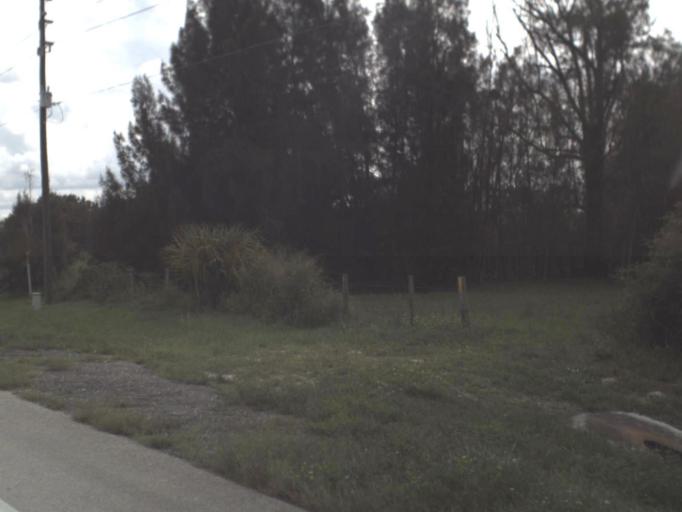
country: US
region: Florida
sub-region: DeSoto County
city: Southeast Arcadia
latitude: 27.1432
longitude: -81.8004
